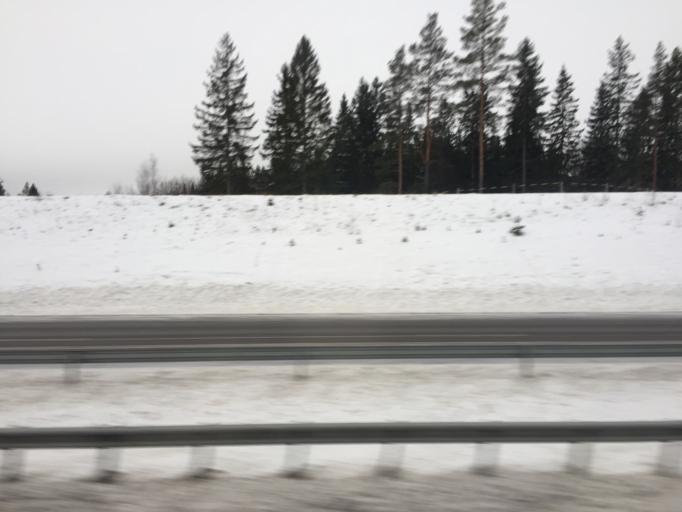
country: FI
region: Kymenlaakso
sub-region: Kotka-Hamina
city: Broby
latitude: 60.4998
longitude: 26.8146
